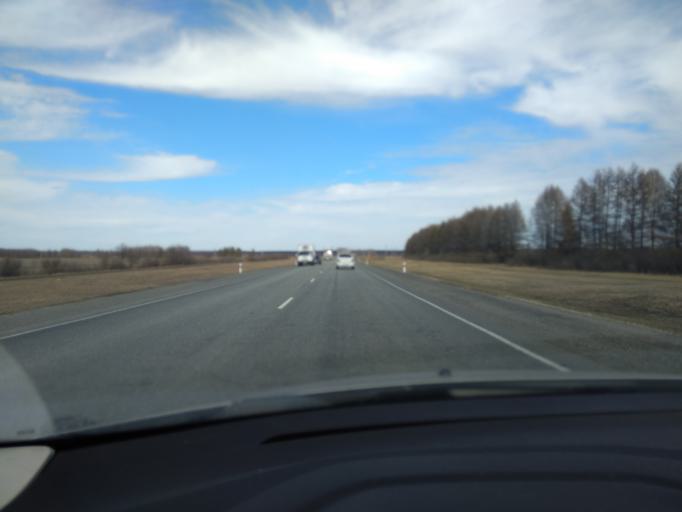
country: RU
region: Sverdlovsk
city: Pyshma
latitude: 57.0395
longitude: 63.4289
